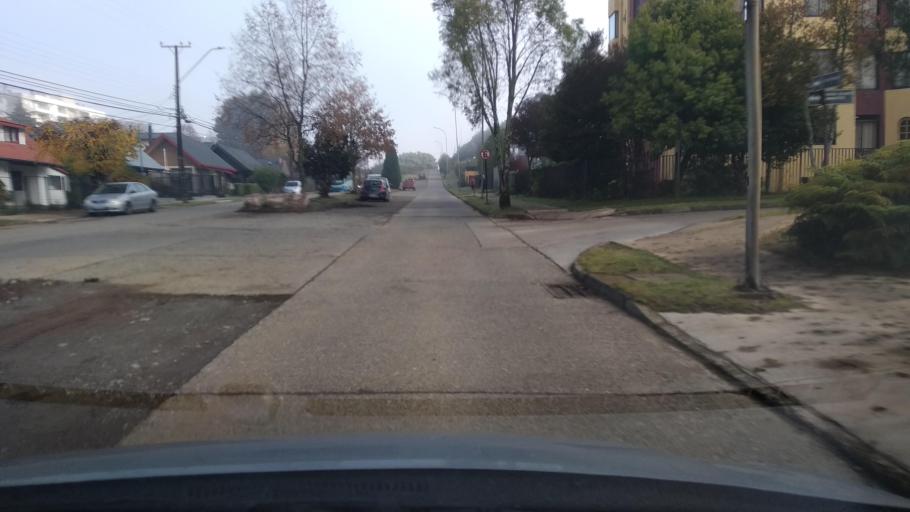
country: CL
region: Los Rios
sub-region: Provincia de Valdivia
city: Valdivia
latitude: -39.8078
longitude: -73.2651
